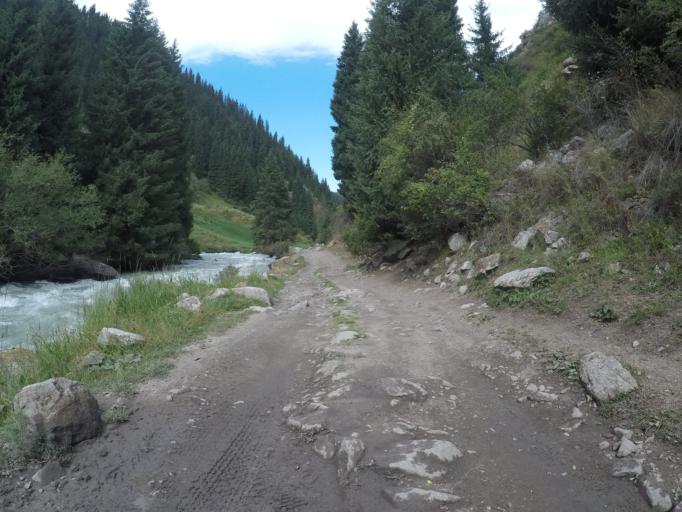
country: KG
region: Ysyk-Koel
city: Teploklyuchenka
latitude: 42.4435
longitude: 78.5507
